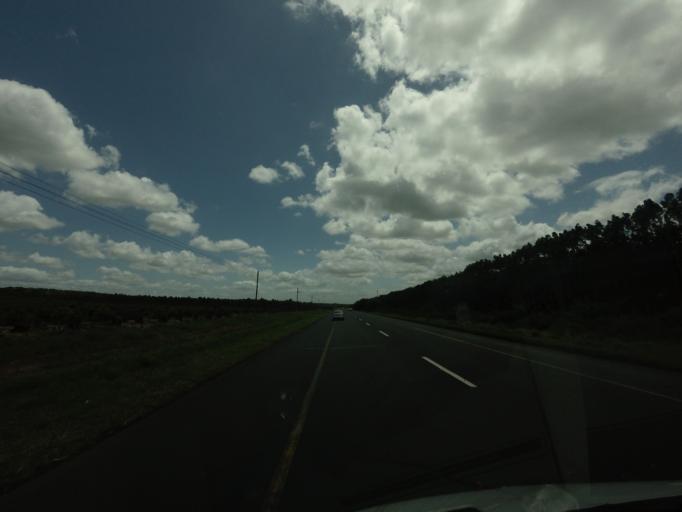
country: ZA
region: KwaZulu-Natal
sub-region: uThungulu District Municipality
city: KwaMbonambi
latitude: -28.5587
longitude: 32.1166
